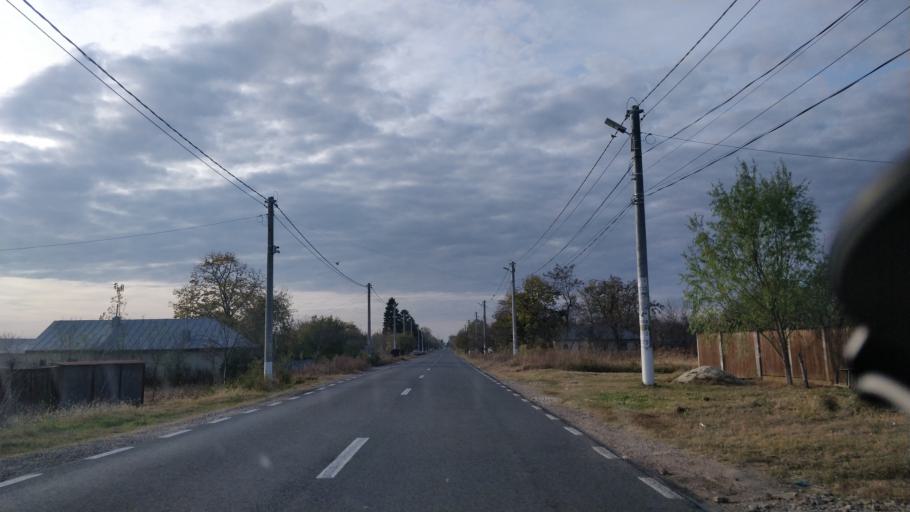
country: RO
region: Giurgiu
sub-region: Comuna Clejani
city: Clejani
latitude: 44.3395
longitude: 25.6857
